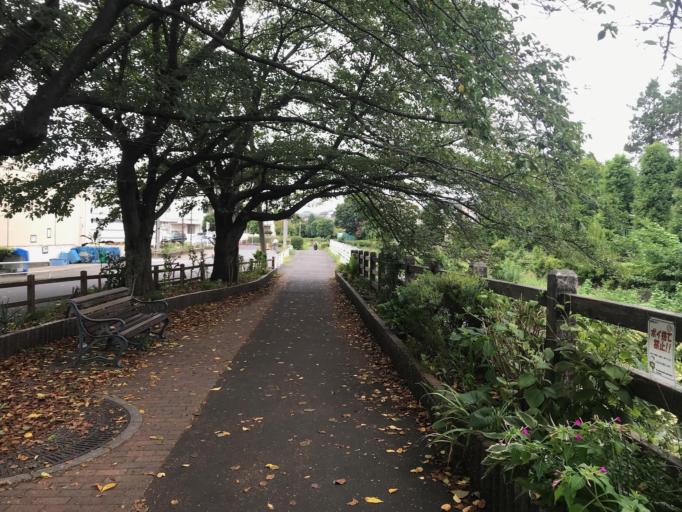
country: JP
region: Tokyo
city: Tanashicho
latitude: 35.7649
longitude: 139.5416
